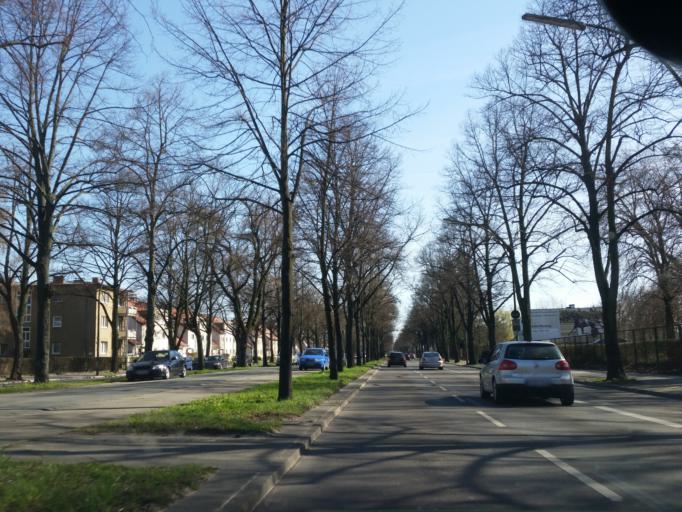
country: DE
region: Berlin
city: Mariendorf
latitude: 52.4295
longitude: 13.3926
